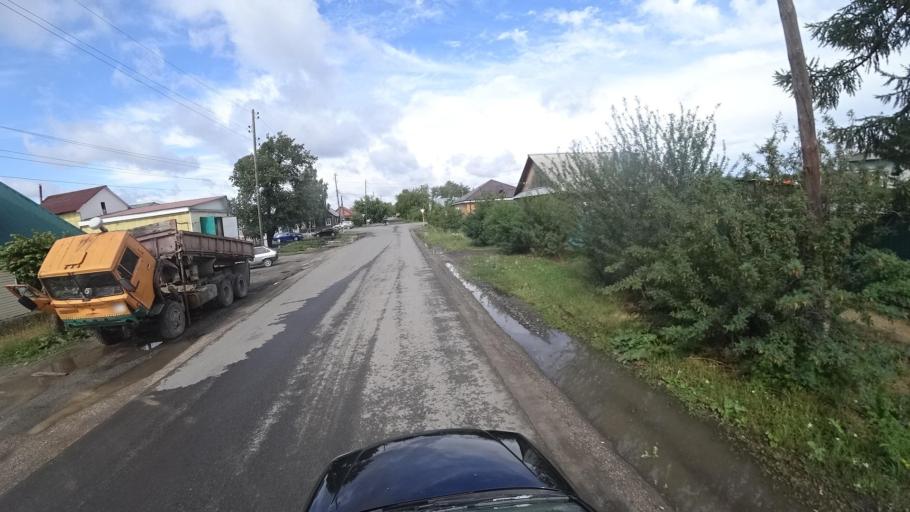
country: RU
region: Sverdlovsk
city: Kamyshlov
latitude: 56.8386
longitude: 62.7297
